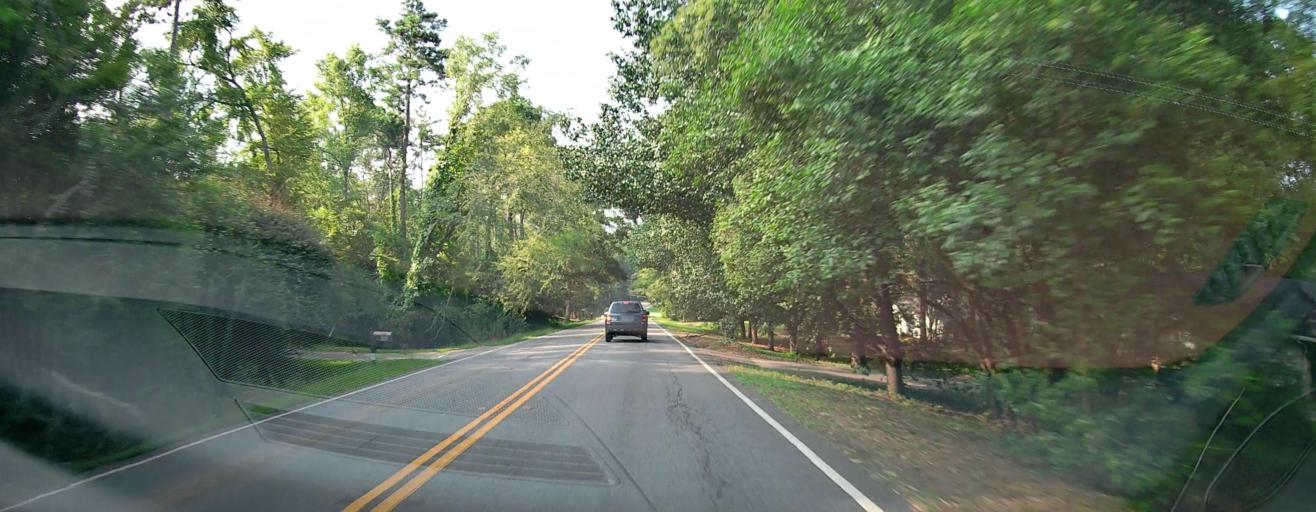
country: US
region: Georgia
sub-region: Bibb County
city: Macon
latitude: 32.8586
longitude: -83.6623
